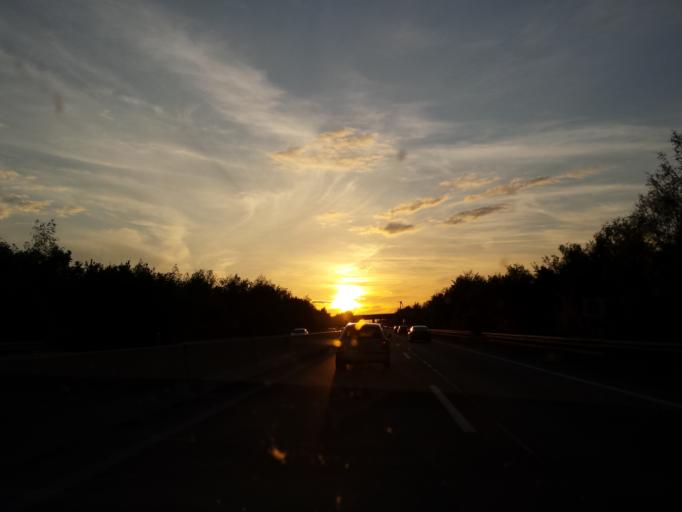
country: AT
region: Burgenland
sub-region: Politischer Bezirk Neusiedl am See
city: Bruckneudorf
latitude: 48.0378
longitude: 16.8066
